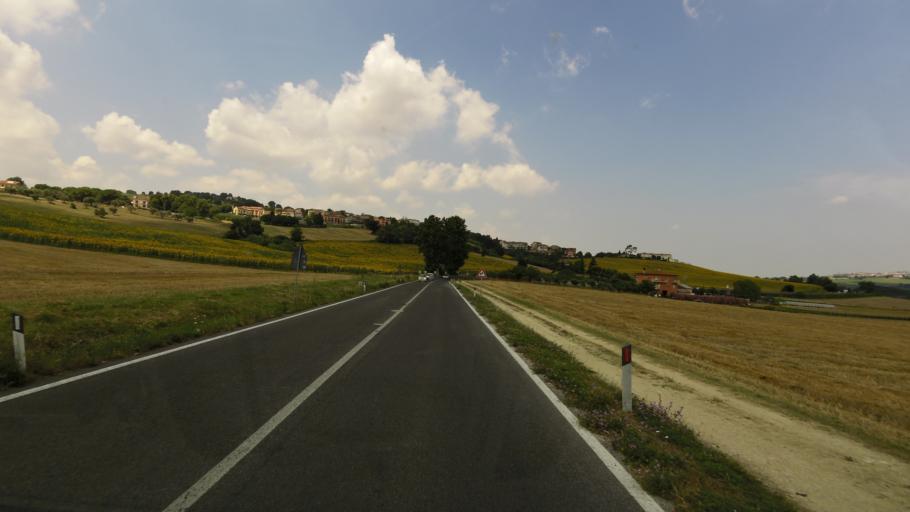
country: IT
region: The Marches
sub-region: Provincia di Ancona
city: Castelfidardo
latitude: 43.4842
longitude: 13.5772
